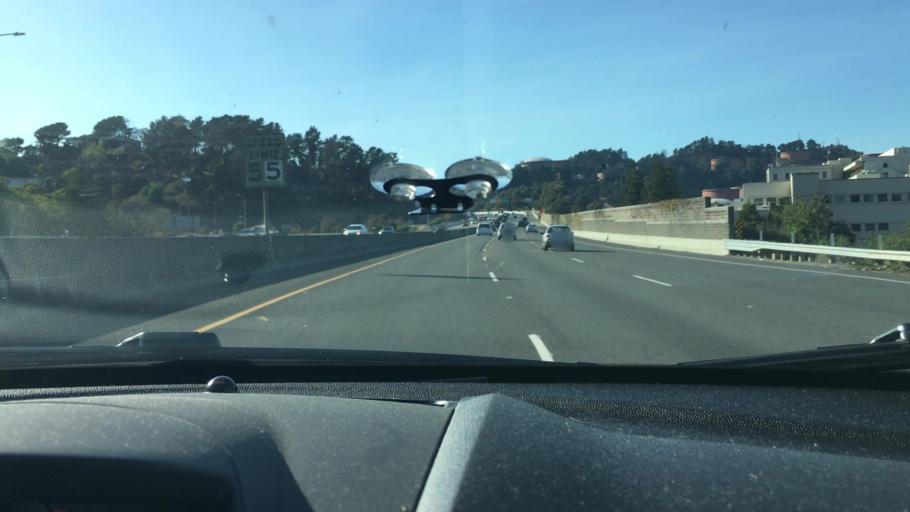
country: US
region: California
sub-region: Contra Costa County
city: North Richmond
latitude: 37.9299
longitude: -122.3887
